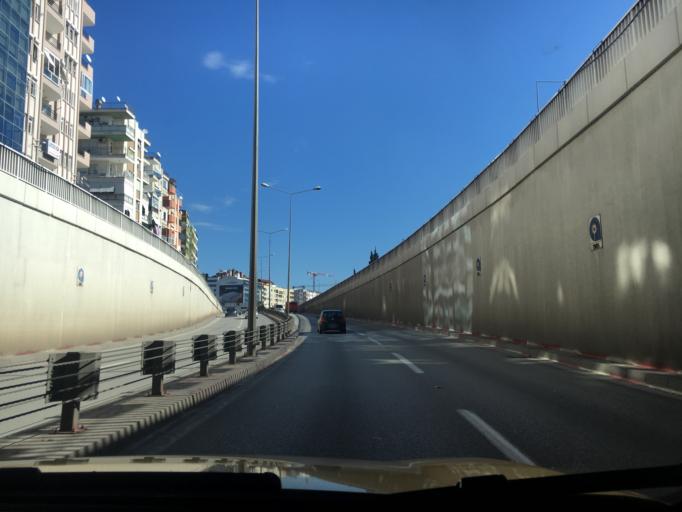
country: TR
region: Antalya
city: Antalya
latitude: 36.8940
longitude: 30.7051
